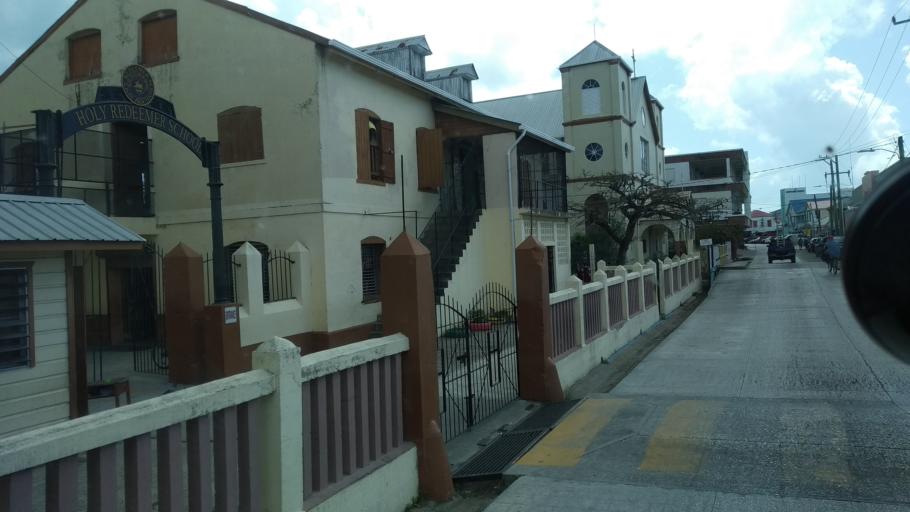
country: BZ
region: Belize
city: Belize City
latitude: 17.4966
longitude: -88.1876
